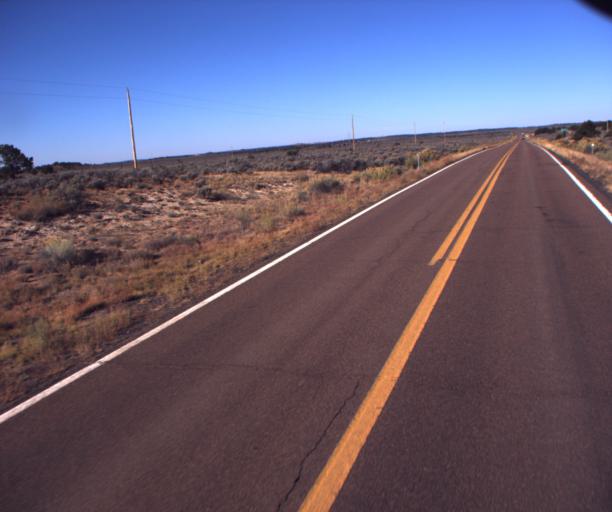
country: US
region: Arizona
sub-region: Apache County
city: Ganado
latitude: 35.7483
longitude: -109.9218
